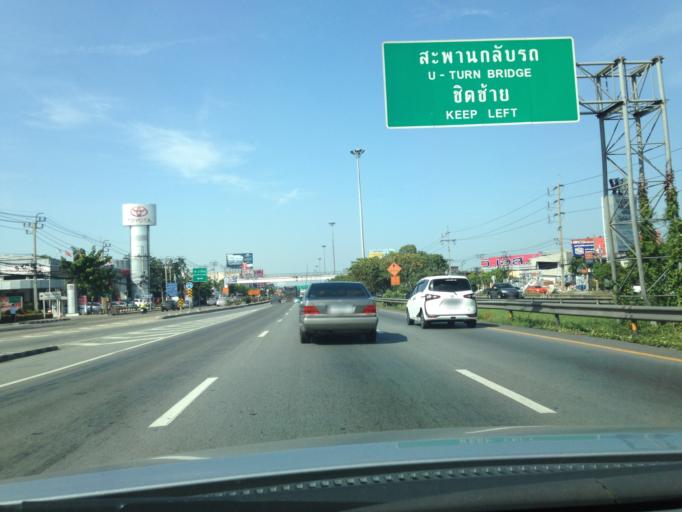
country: TH
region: Nonthaburi
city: Bang Yai
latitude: 13.8430
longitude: 100.4128
